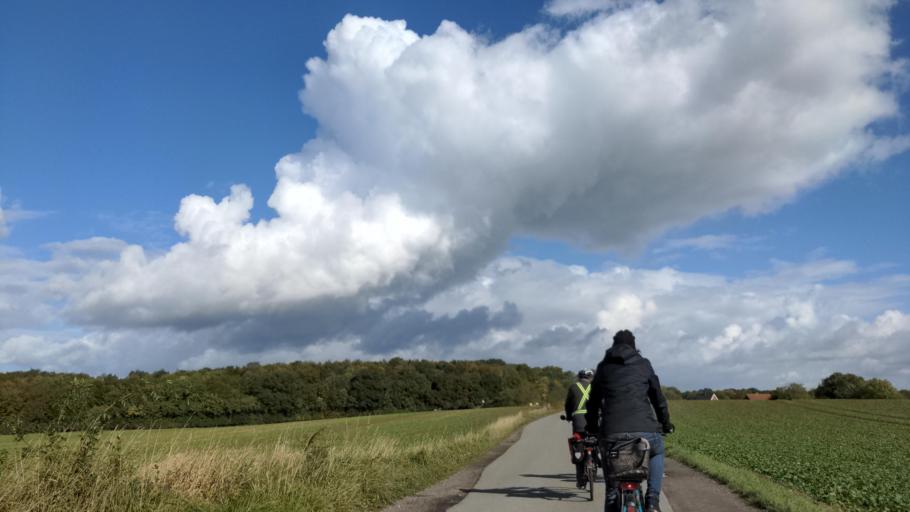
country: DE
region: Schleswig-Holstein
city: Heidekamp
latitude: 53.8399
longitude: 10.5162
